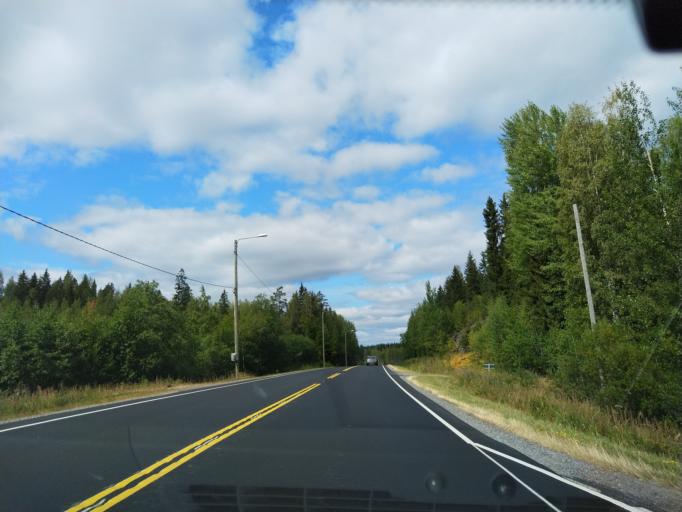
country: FI
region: Haeme
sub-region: Riihimaeki
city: Loppi
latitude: 60.7158
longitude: 24.4679
